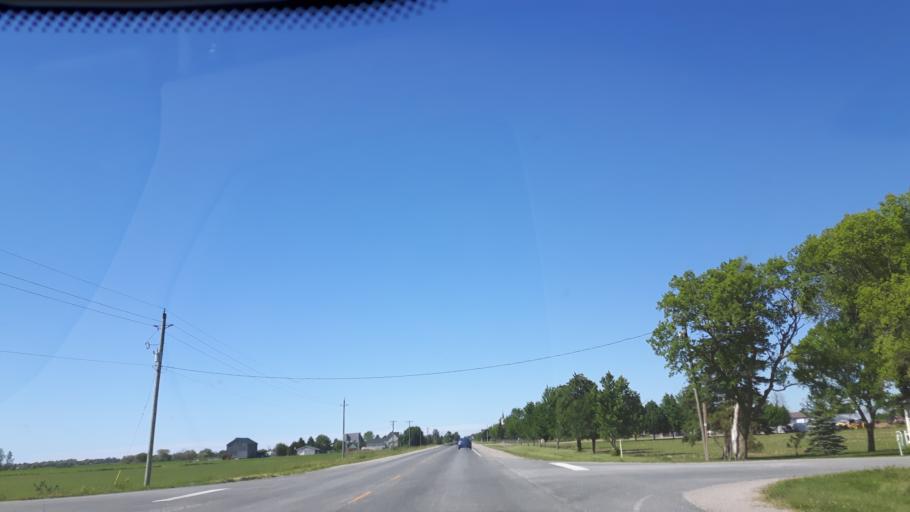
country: CA
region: Ontario
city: Bluewater
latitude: 43.4314
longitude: -81.7038
